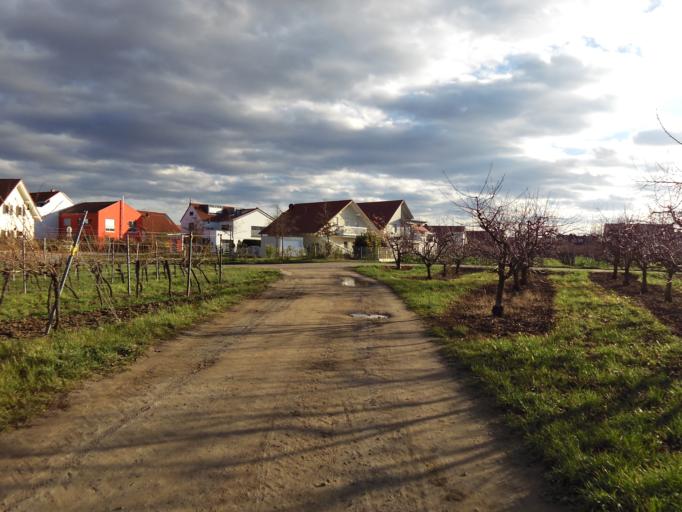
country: DE
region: Rheinland-Pfalz
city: Erpolzheim
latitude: 49.4912
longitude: 8.2187
